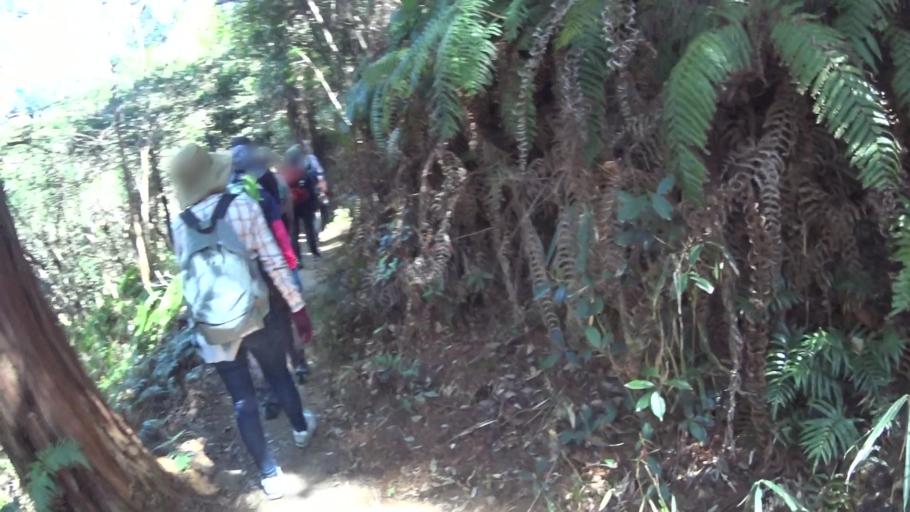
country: JP
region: Kyoto
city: Kyoto
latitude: 34.9848
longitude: 135.7862
